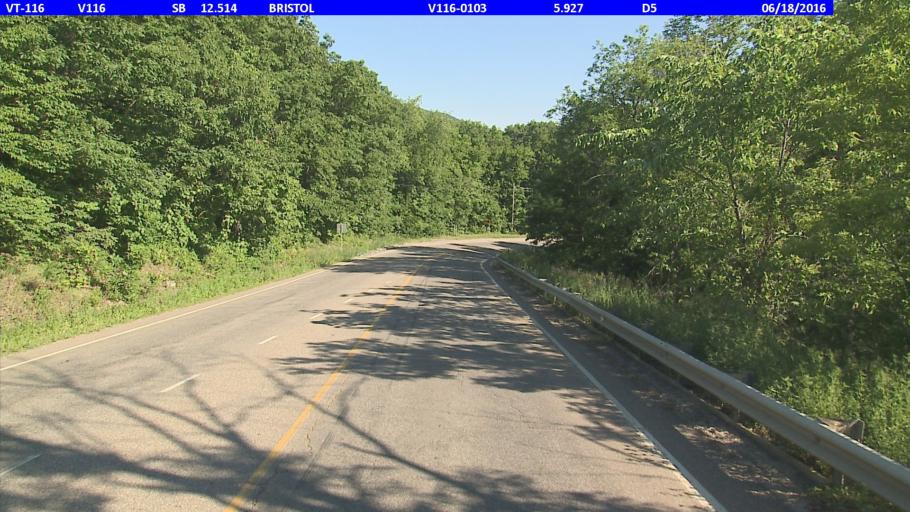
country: US
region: Vermont
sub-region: Addison County
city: Bristol
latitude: 44.1315
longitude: -73.0901
